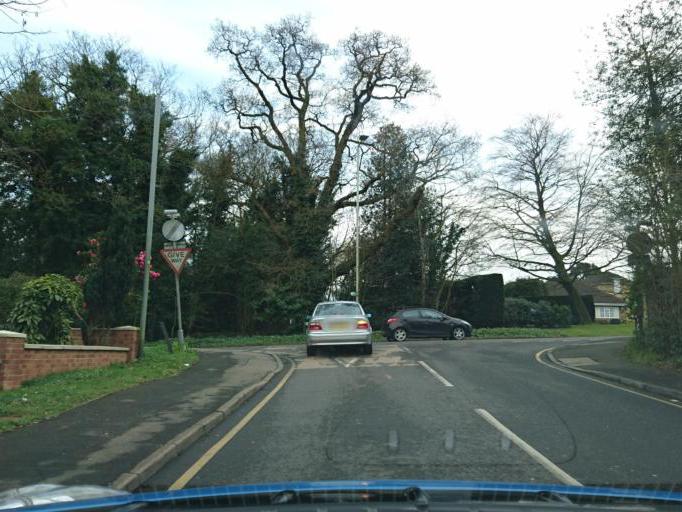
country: GB
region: England
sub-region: Hertfordshire
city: Borehamwood
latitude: 51.6450
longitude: -0.2798
